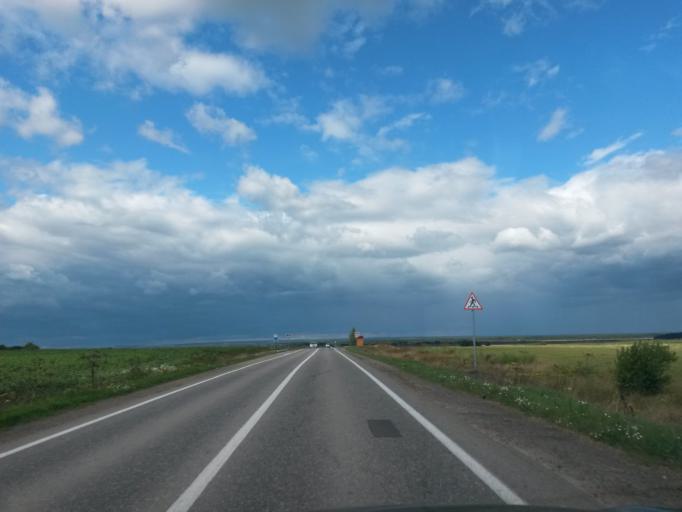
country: RU
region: Jaroslavl
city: Yaroslavl
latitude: 57.7579
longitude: 39.8692
